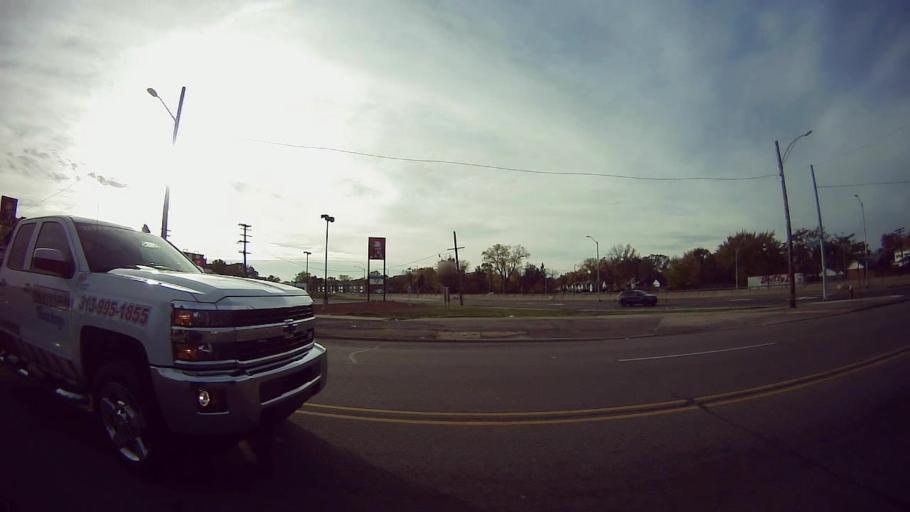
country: US
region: Michigan
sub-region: Oakland County
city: Oak Park
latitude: 42.4309
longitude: -83.1861
